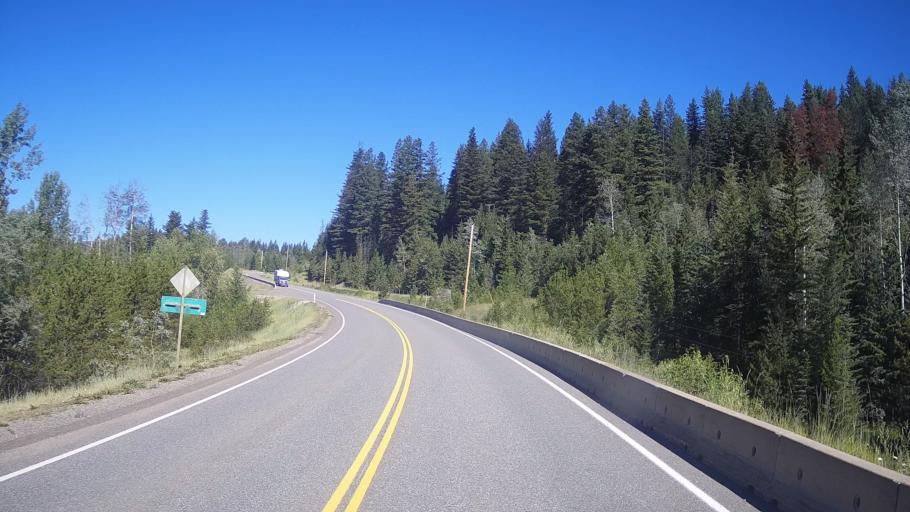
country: CA
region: British Columbia
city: Kamloops
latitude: 51.4756
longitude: -120.5569
